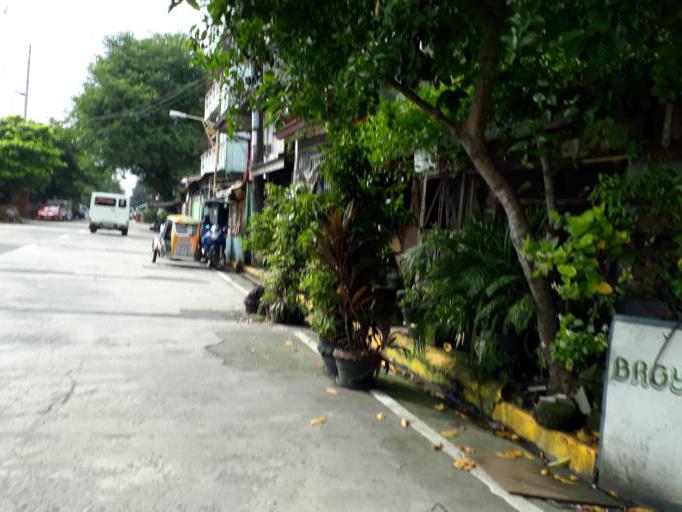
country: PH
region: Metro Manila
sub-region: City of Manila
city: Manila
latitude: 14.6086
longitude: 121.0006
